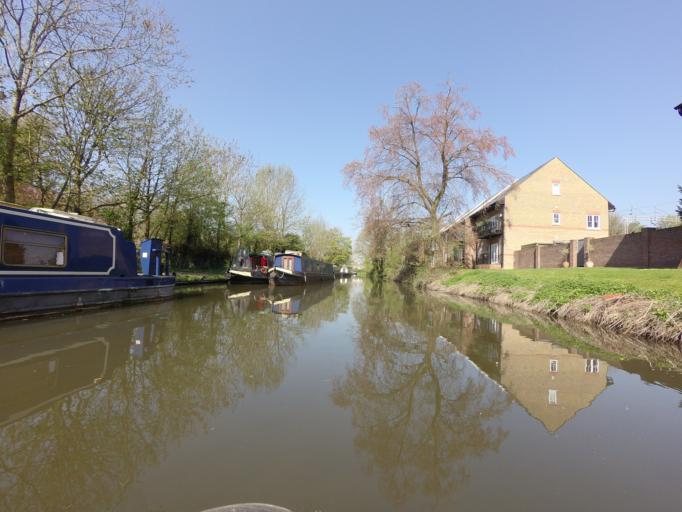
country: GB
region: England
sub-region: Hertfordshire
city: Berkhamsted
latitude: 51.7563
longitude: -0.5475
